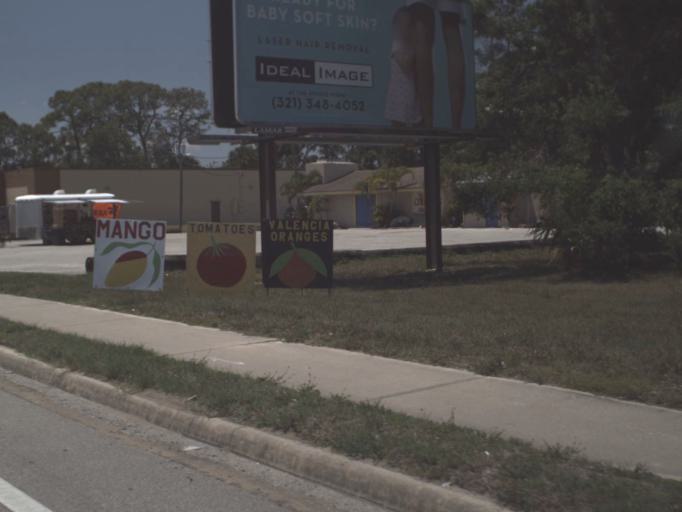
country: US
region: Florida
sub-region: Brevard County
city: June Park
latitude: 28.0790
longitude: -80.6920
